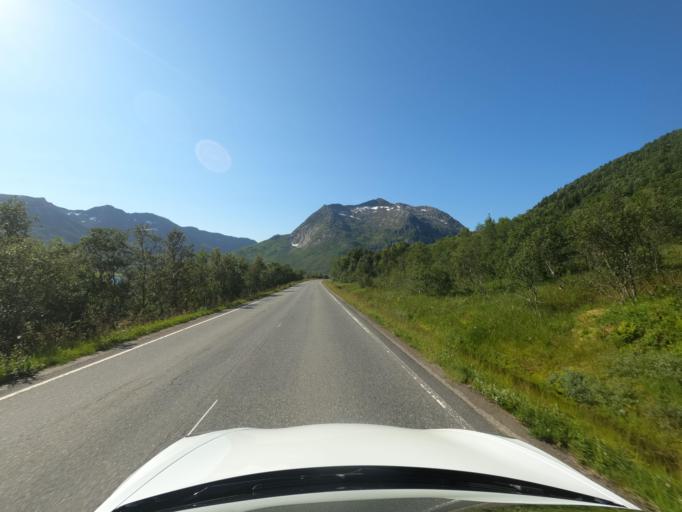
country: NO
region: Nordland
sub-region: Lodingen
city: Lodingen
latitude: 68.5484
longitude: 15.7450
